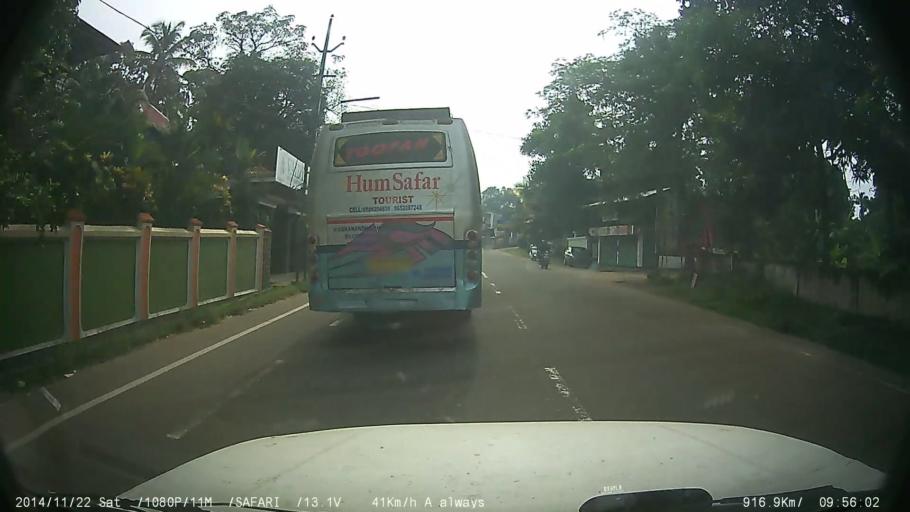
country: IN
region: Kerala
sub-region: Ernakulam
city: Perumbavoor
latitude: 10.1030
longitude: 76.4851
